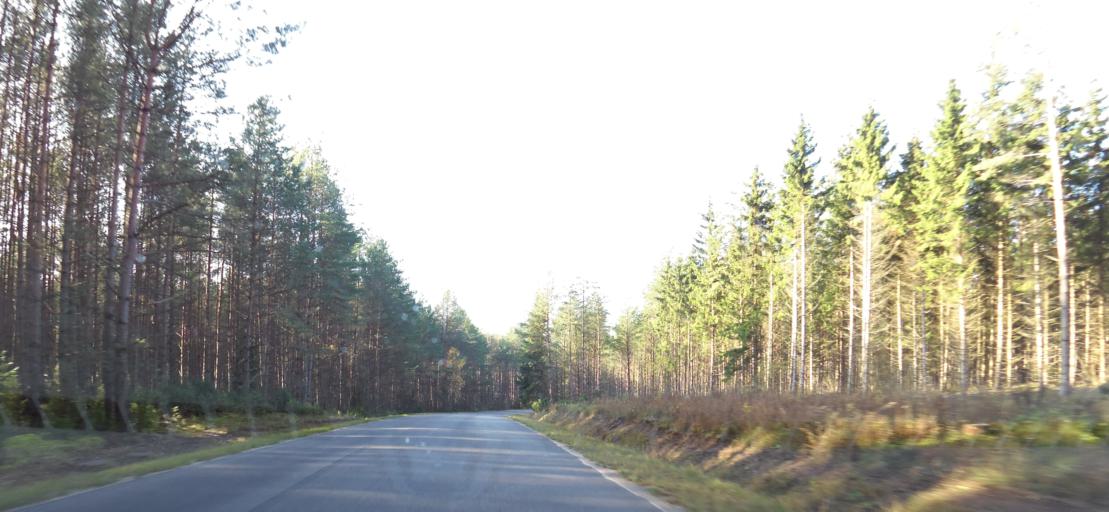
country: LT
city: Trakai
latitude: 54.5300
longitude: 24.9775
